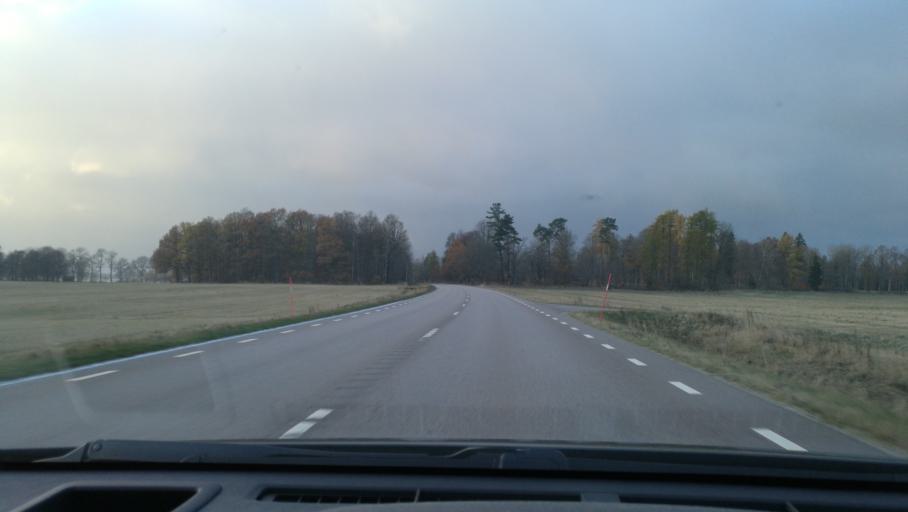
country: SE
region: Soedermanland
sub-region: Vingakers Kommun
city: Vingaker
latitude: 59.1565
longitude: 16.0285
